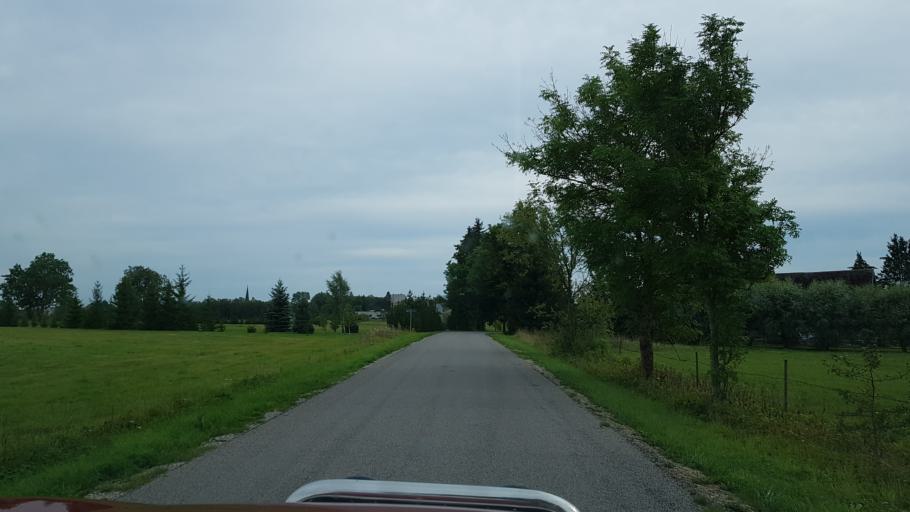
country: EE
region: Laeaene
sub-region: Ridala Parish
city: Uuemoisa
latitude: 58.9735
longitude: 23.7708
